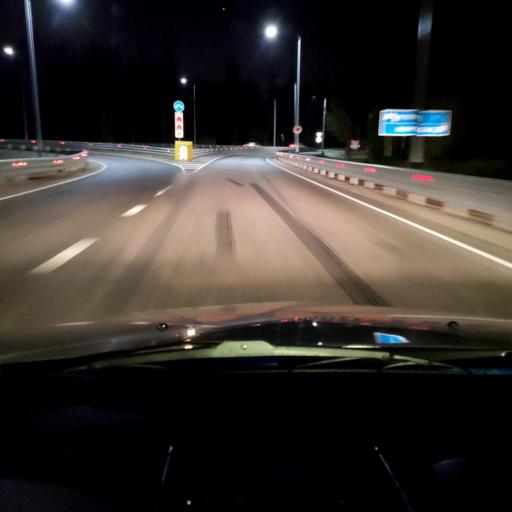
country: RU
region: Voronezj
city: Somovo
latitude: 51.6917
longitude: 39.3002
